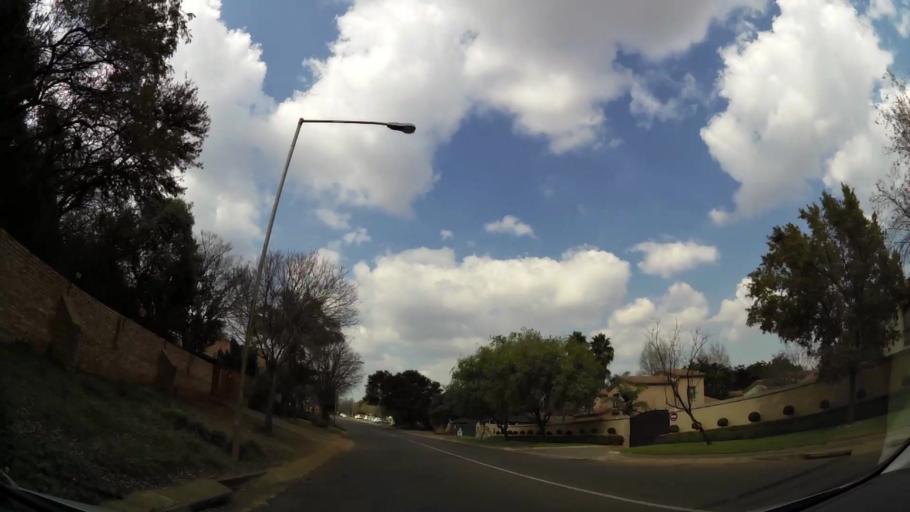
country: ZA
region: Gauteng
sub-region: City of Tshwane Metropolitan Municipality
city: Pretoria
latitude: -25.7873
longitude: 28.3205
